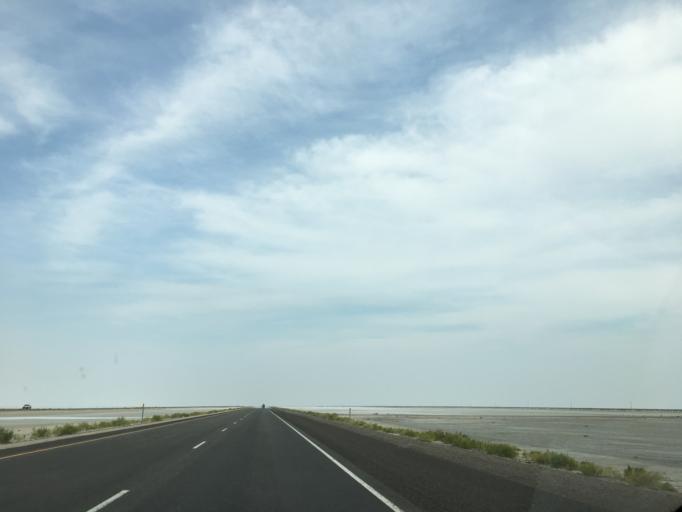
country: US
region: Utah
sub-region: Tooele County
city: Wendover
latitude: 40.7366
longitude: -113.7574
